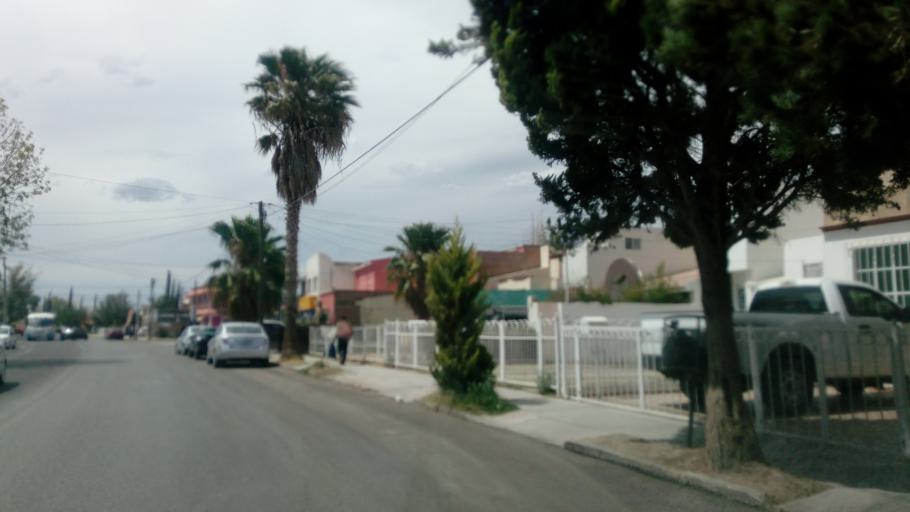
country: MX
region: Durango
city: Victoria de Durango
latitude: 23.9959
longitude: -104.6473
